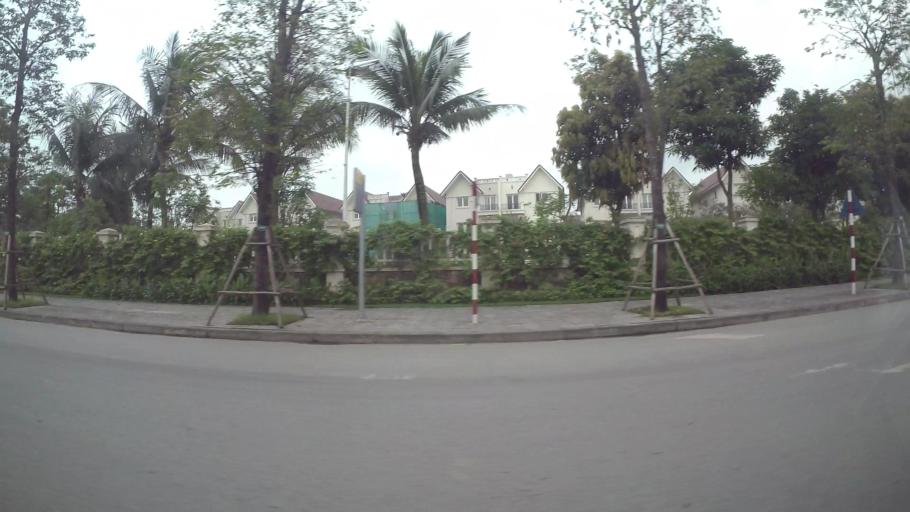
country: VN
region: Ha Noi
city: Trau Quy
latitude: 21.0387
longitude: 105.9226
